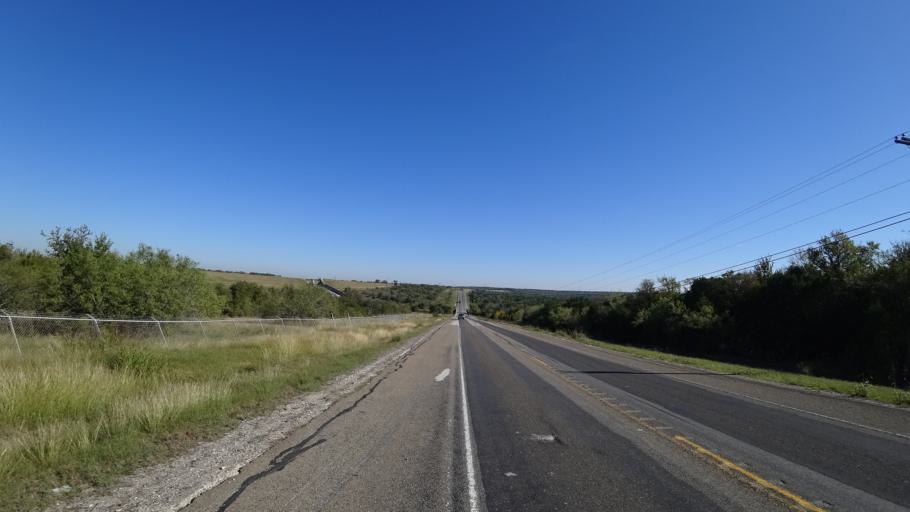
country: US
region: Texas
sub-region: Travis County
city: Hornsby Bend
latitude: 30.2792
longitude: -97.5978
